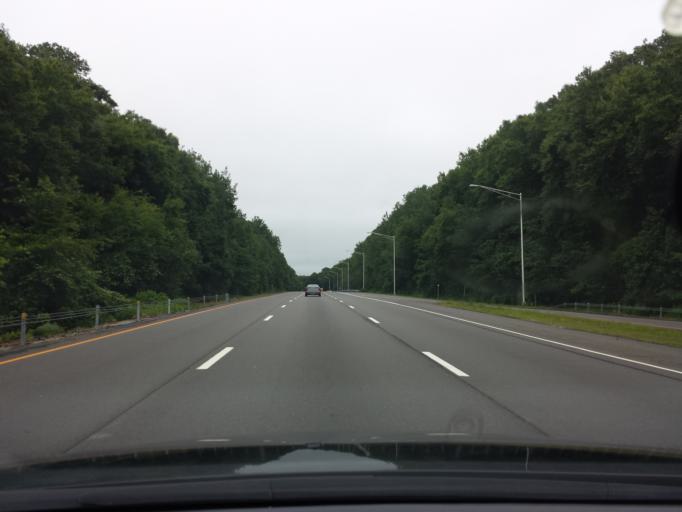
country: US
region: Connecticut
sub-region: New London County
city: Poquonock Bridge
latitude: 41.3617
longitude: -72.0243
